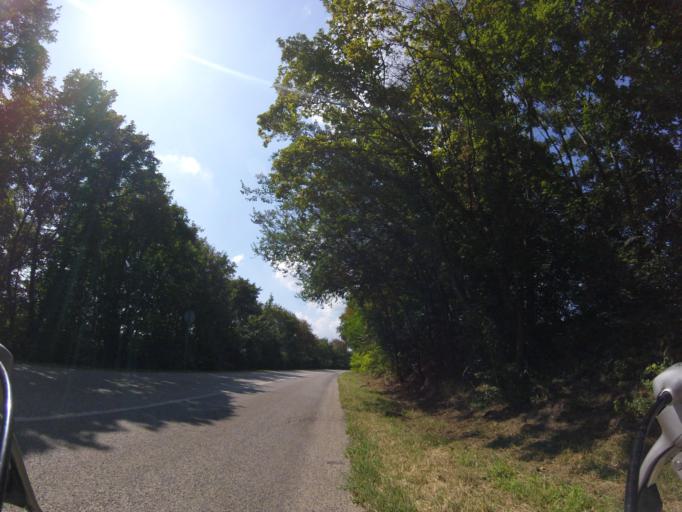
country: HU
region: Fejer
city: Etyek
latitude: 47.4841
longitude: 18.7709
